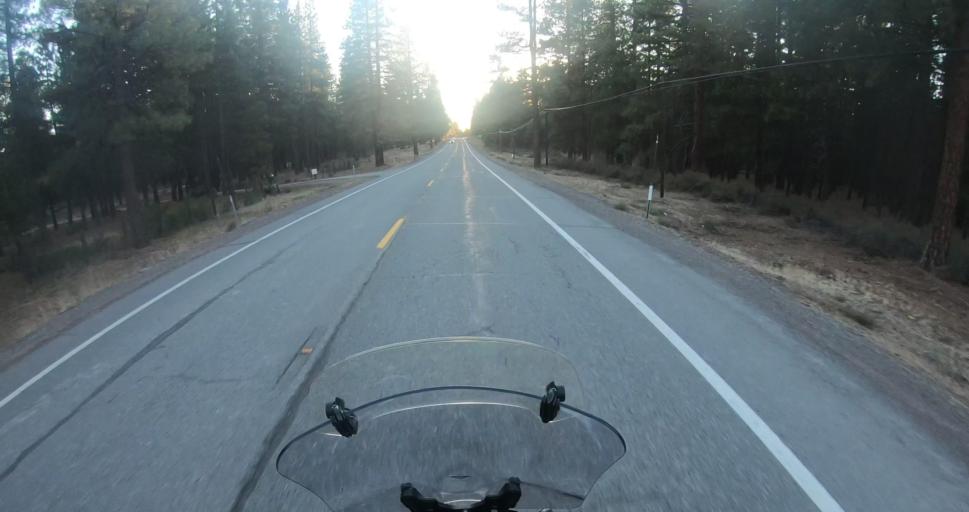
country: US
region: California
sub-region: Lassen County
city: Susanville
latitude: 40.4163
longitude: -120.7200
